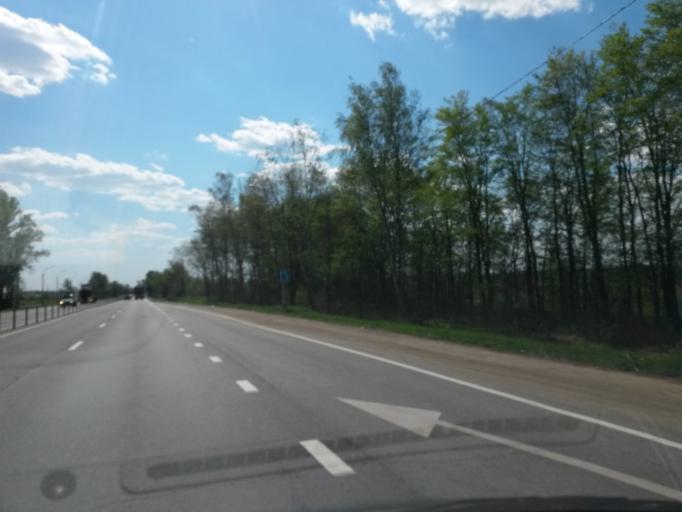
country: RU
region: Jaroslavl
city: Semibratovo
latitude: 57.3273
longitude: 39.5694
